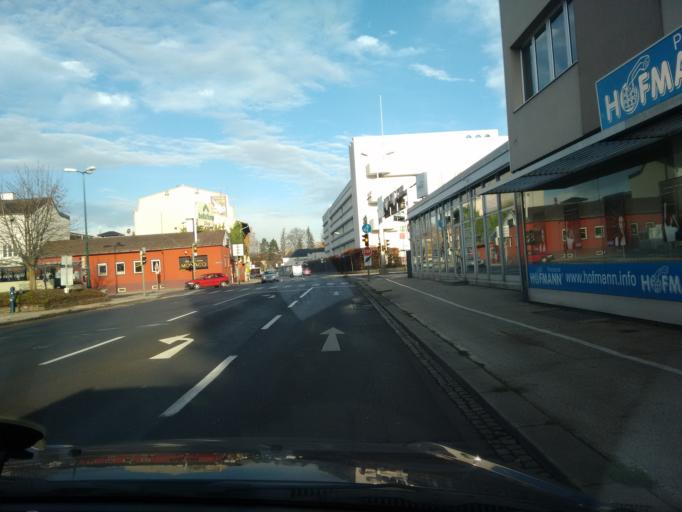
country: AT
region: Upper Austria
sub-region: Wels Stadt
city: Wels
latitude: 48.1600
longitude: 14.0193
